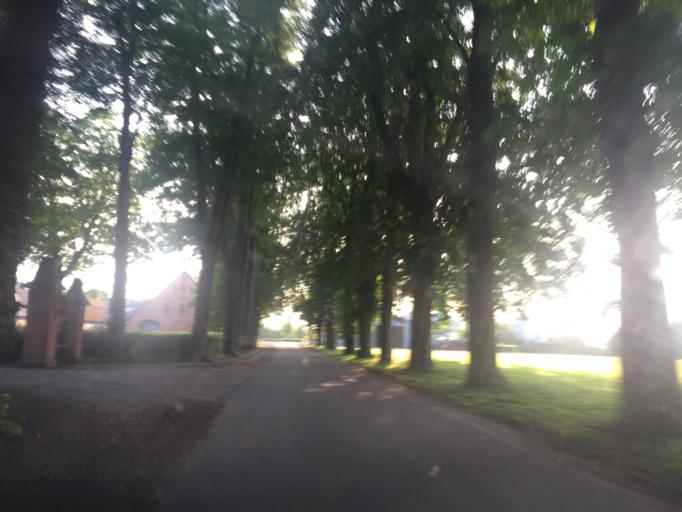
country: DK
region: South Denmark
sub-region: Kerteminde Kommune
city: Langeskov
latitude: 55.3538
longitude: 10.5331
